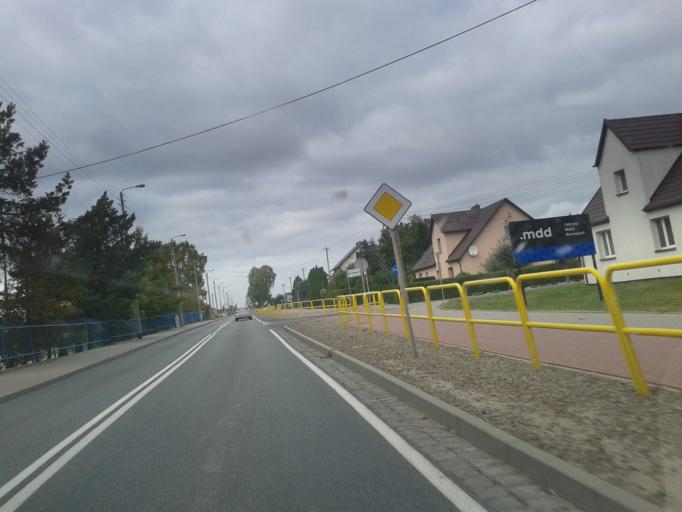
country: PL
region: Kujawsko-Pomorskie
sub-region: Powiat sepolenski
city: Sepolno Krajenskie
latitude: 53.4612
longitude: 17.5314
